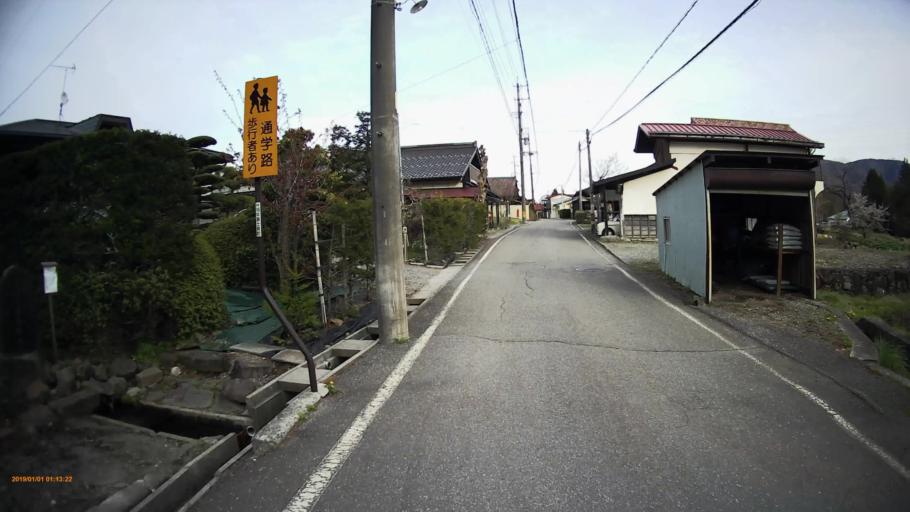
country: JP
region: Nagano
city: Chino
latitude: 35.9128
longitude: 138.2218
